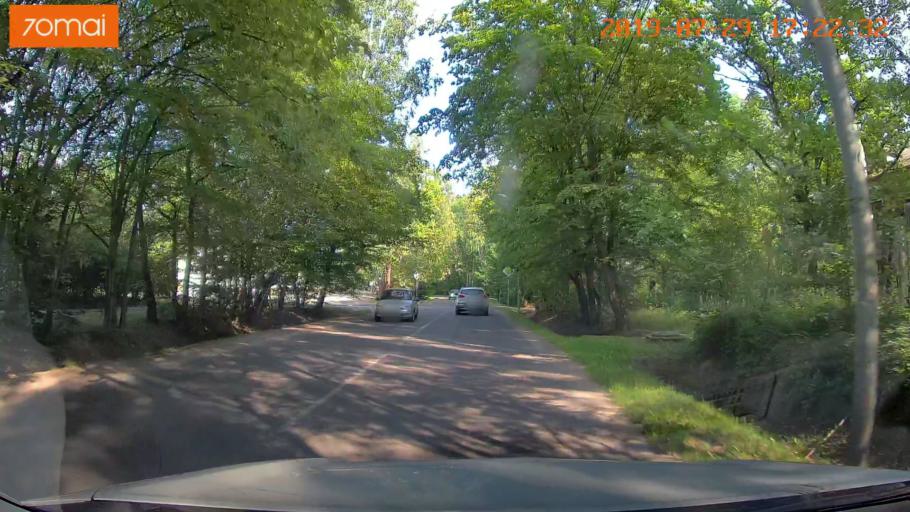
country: RU
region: Kaliningrad
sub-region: Gorod Kaliningrad
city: Kaliningrad
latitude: 54.7685
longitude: 20.4446
